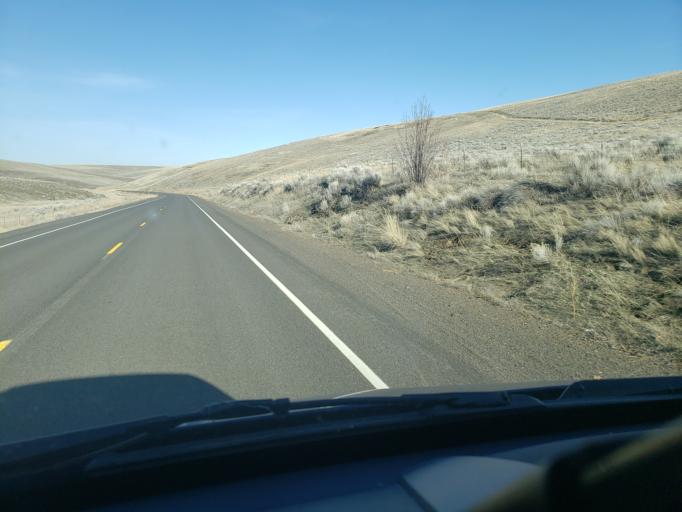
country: US
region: Oregon
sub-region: Umatilla County
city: Pilot Rock
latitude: 45.4599
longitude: -118.9341
